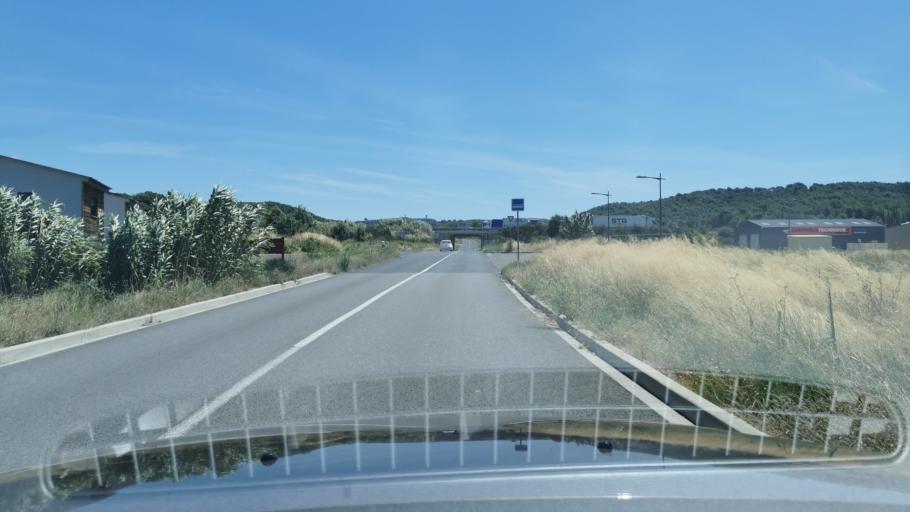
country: FR
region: Languedoc-Roussillon
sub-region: Departement de l'Aude
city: Vinassan
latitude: 43.1965
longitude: 3.0721
